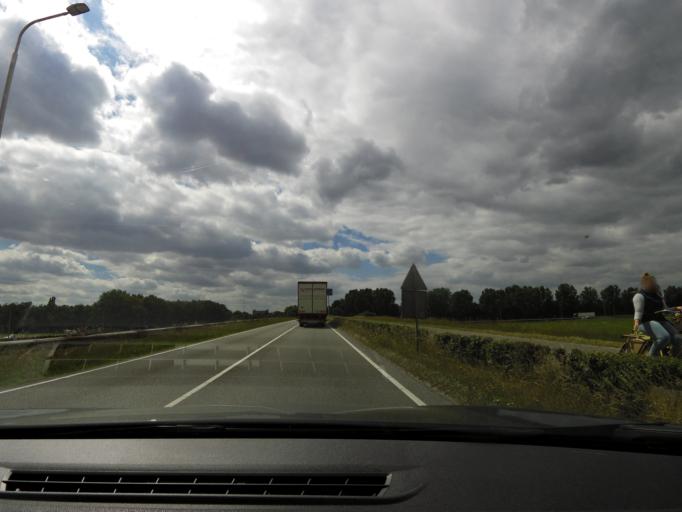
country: NL
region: North Brabant
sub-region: Gemeente Oosterhout
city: Oosterhout
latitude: 51.6497
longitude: 4.8856
